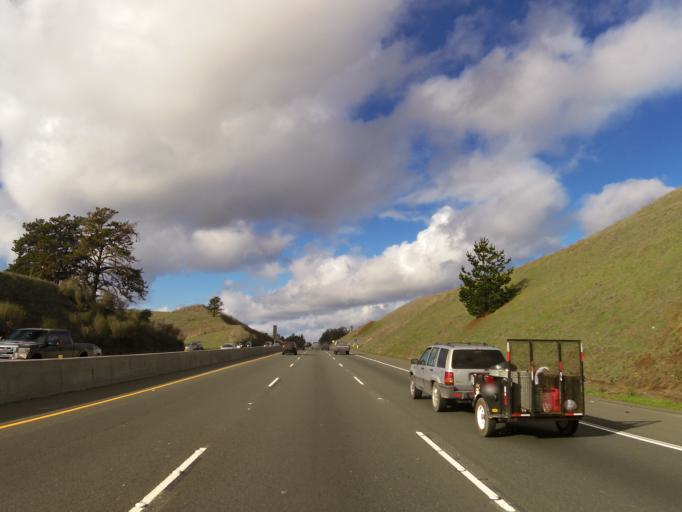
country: US
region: California
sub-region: Sonoma County
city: Cotati
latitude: 38.2969
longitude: -122.7025
